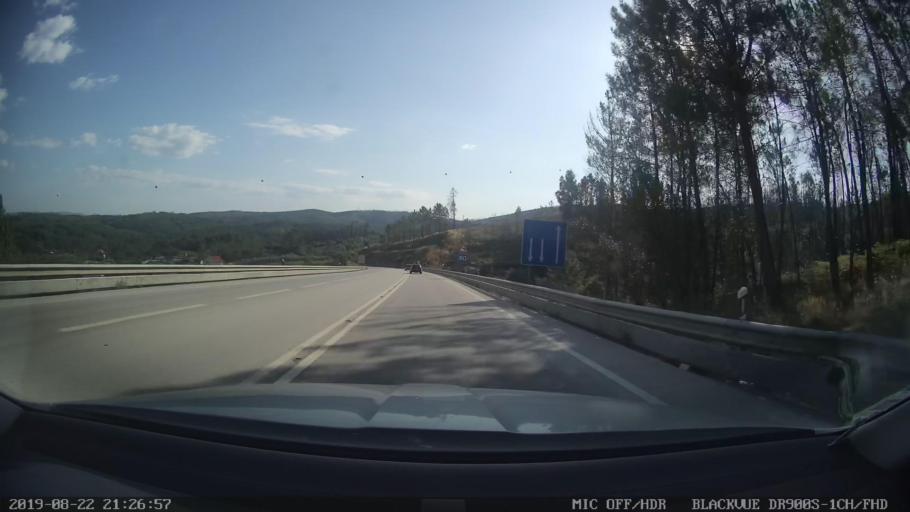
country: PT
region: Leiria
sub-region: Pedrogao Grande
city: Pedrogao Grande
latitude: 39.8721
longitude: -8.1212
